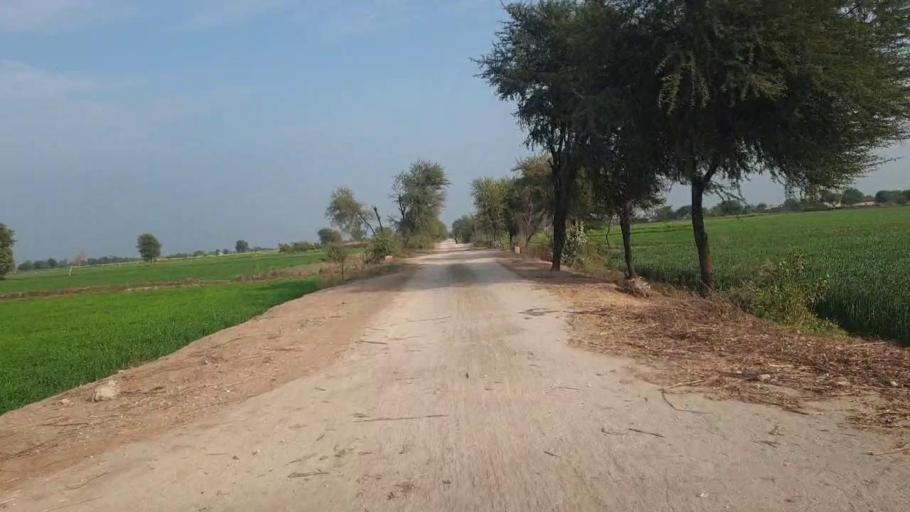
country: PK
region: Sindh
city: Shahdadpur
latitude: 25.8710
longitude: 68.7072
